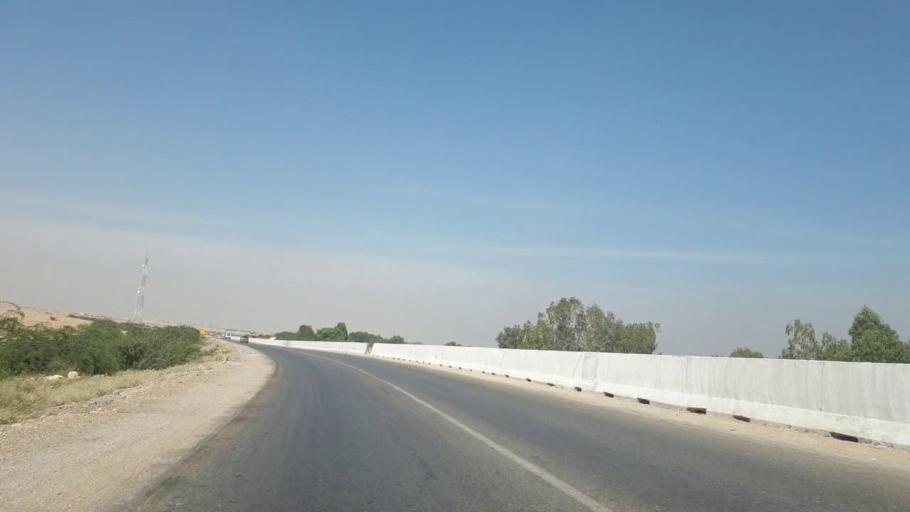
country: PK
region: Sindh
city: Hala
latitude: 25.7137
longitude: 68.2958
